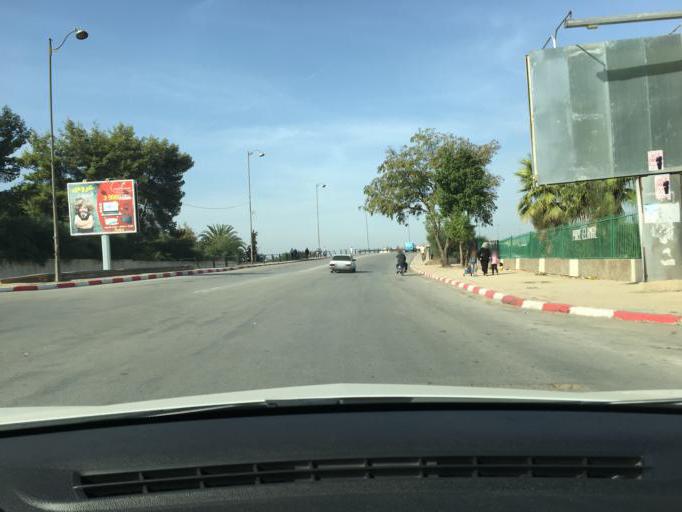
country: MA
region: Fes-Boulemane
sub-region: Fes
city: Fes
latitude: 34.0388
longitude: -5.0225
